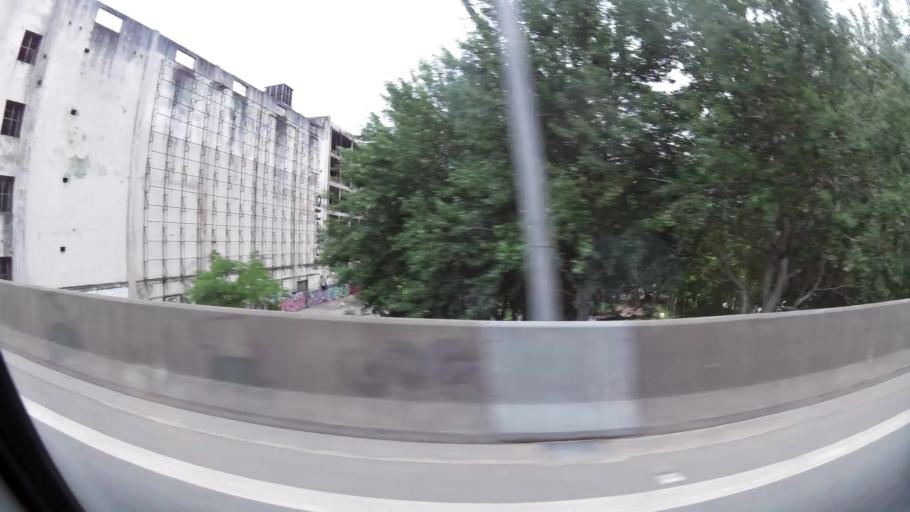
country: AR
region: Buenos Aires F.D.
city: Buenos Aires
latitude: -34.6266
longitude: -58.3598
